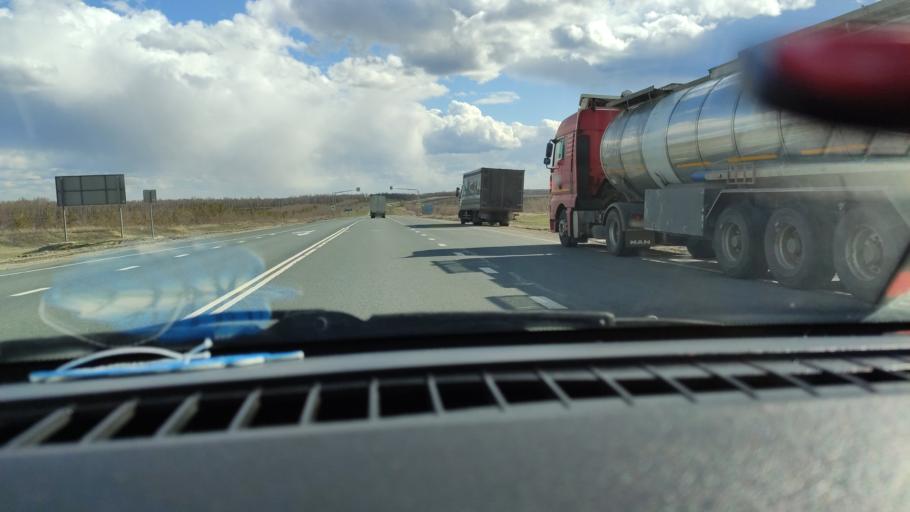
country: RU
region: Saratov
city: Alekseyevka
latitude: 52.2867
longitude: 47.9309
